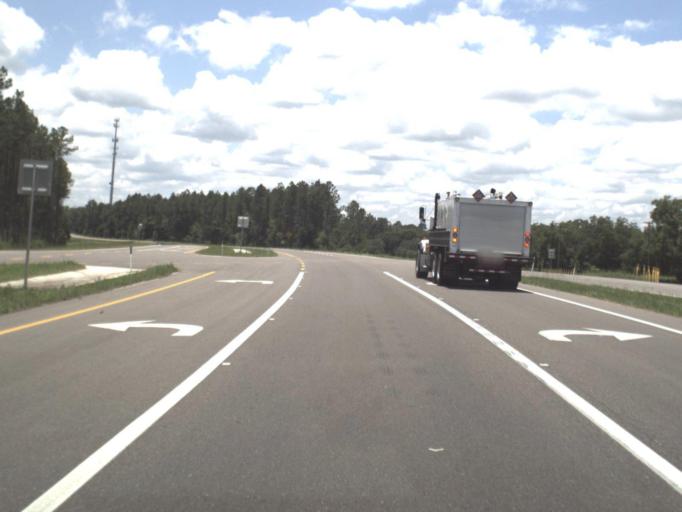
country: US
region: Florida
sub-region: Alachua County
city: Waldo
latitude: 29.7165
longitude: -82.1306
